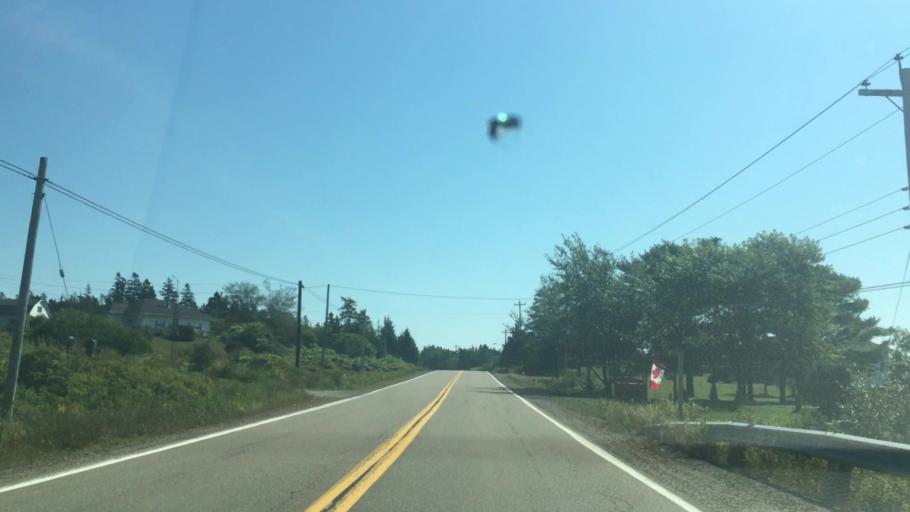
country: CA
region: Nova Scotia
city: Antigonish
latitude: 45.0261
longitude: -62.0274
